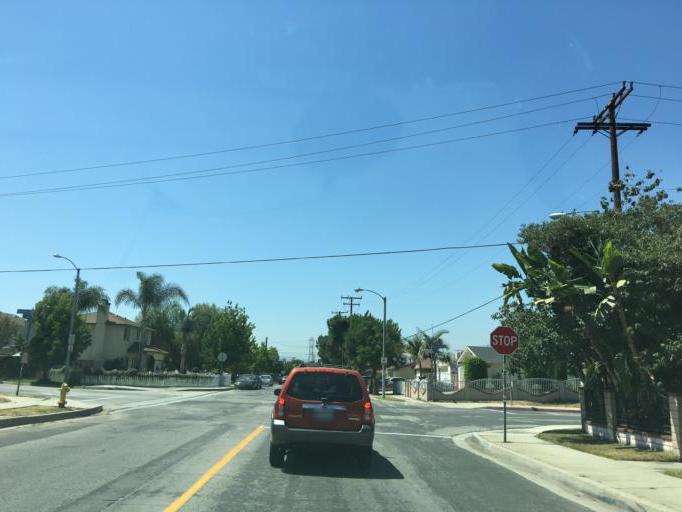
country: US
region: California
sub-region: Los Angeles County
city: Avocado Heights
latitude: 34.0434
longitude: -118.0013
